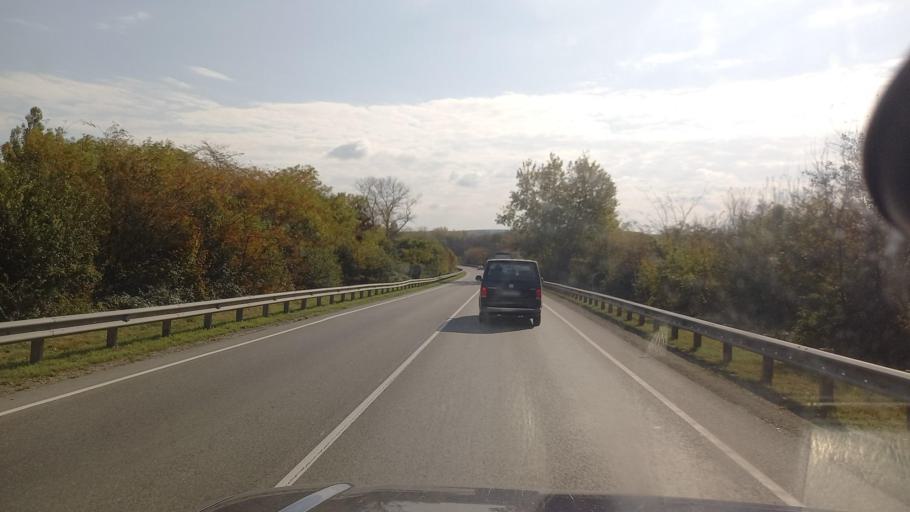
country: RU
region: Krasnodarskiy
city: Abinsk
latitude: 44.8458
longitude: 38.1503
